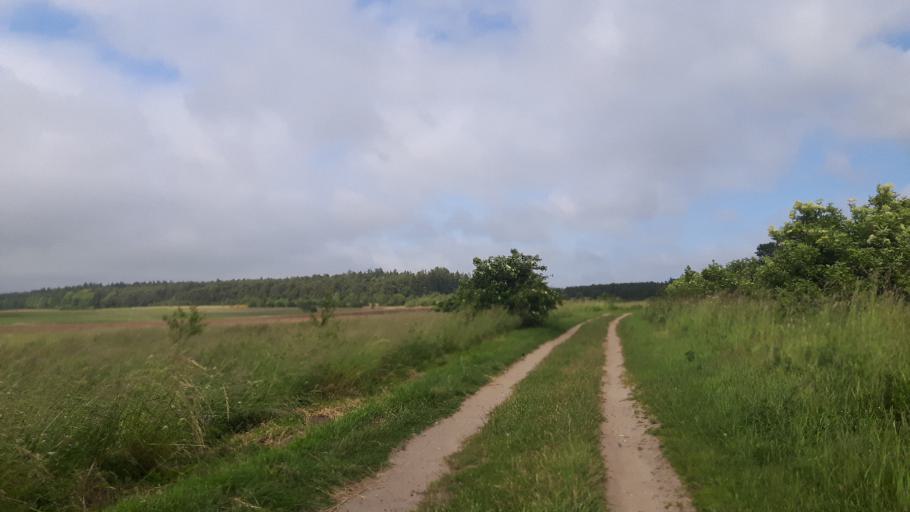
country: PL
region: Pomeranian Voivodeship
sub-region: Slupsk
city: Slupsk
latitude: 54.5994
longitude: 17.0029
